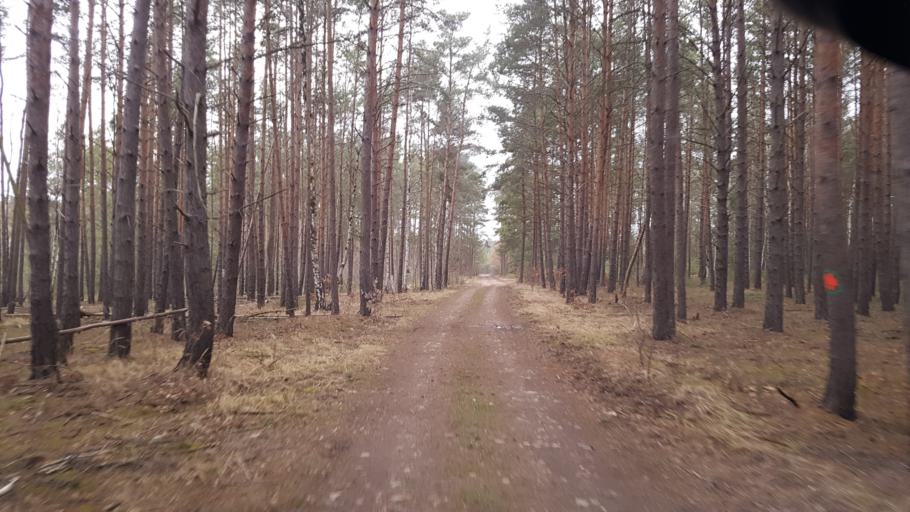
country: DE
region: Brandenburg
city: Trobitz
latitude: 51.6107
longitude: 13.4582
